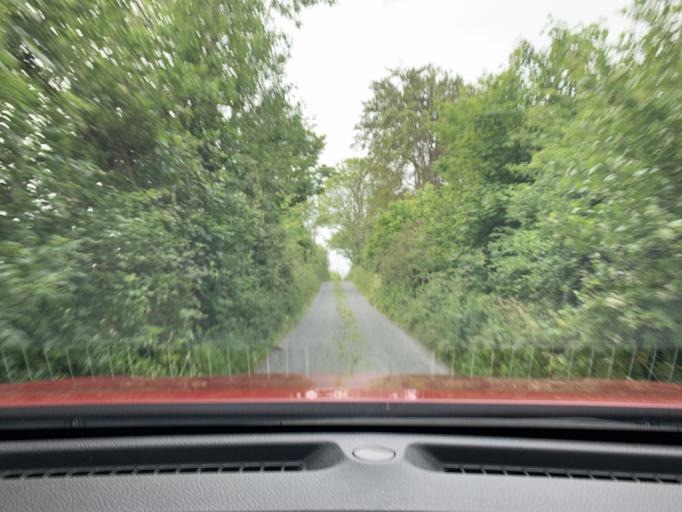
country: IE
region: Connaught
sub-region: Sligo
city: Sligo
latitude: 54.3846
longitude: -8.5227
